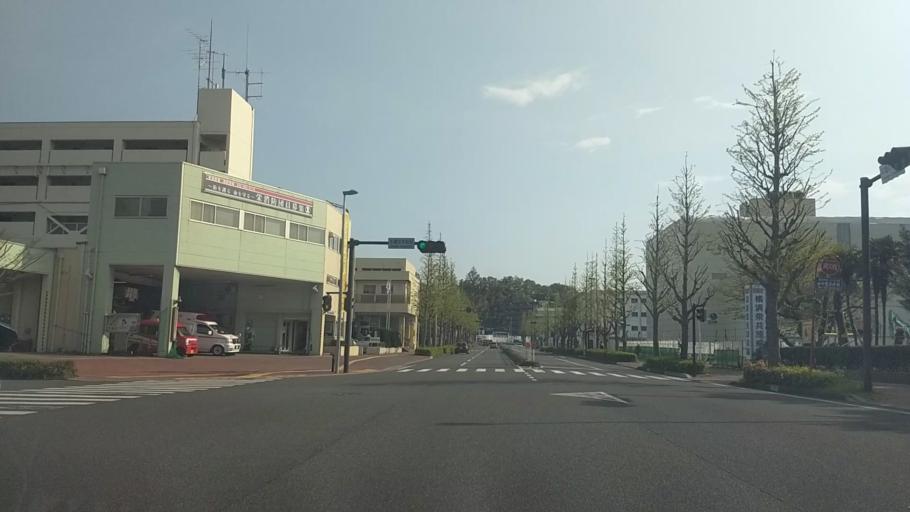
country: JP
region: Kanagawa
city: Kamakura
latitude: 35.3645
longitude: 139.5521
